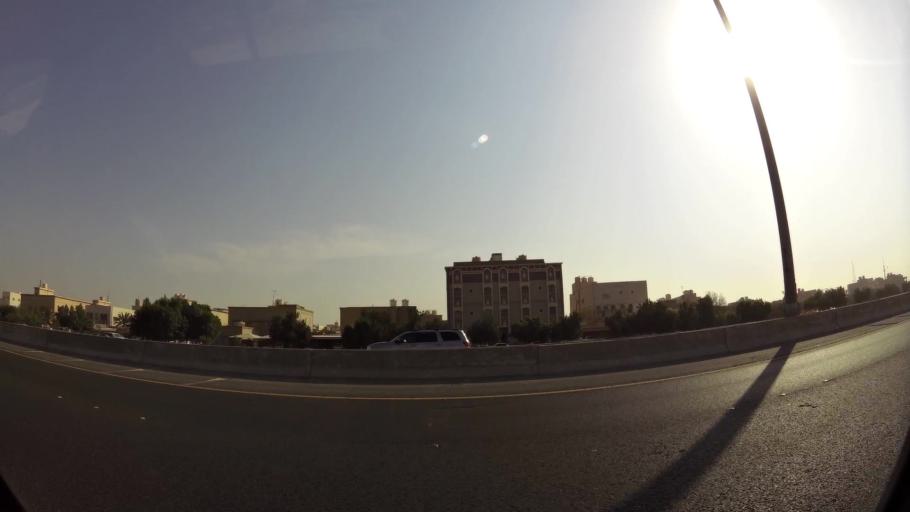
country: KW
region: Al Ahmadi
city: Al Ahmadi
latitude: 29.0964
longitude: 48.0974
